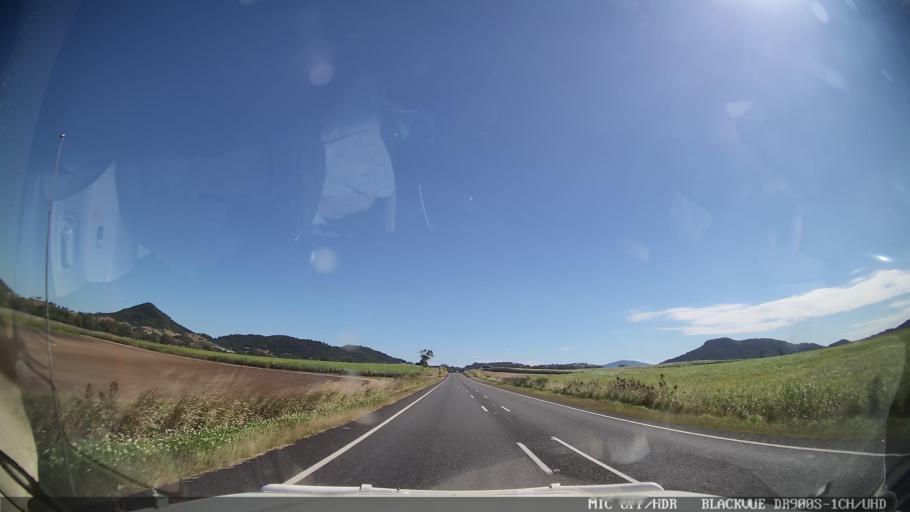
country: AU
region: Queensland
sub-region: Mackay
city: Walkerston
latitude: -21.0905
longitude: 149.0498
